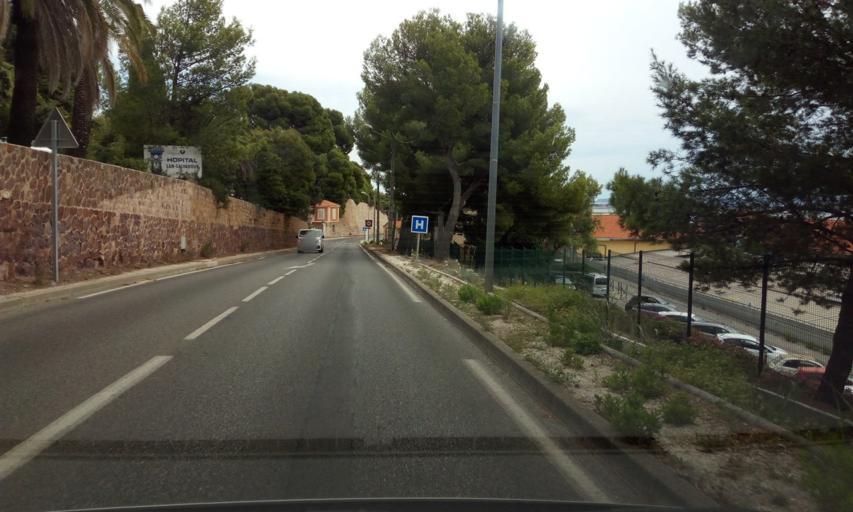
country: FR
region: Provence-Alpes-Cote d'Azur
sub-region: Departement du Var
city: Carqueiranne
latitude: 43.0848
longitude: 6.1099
